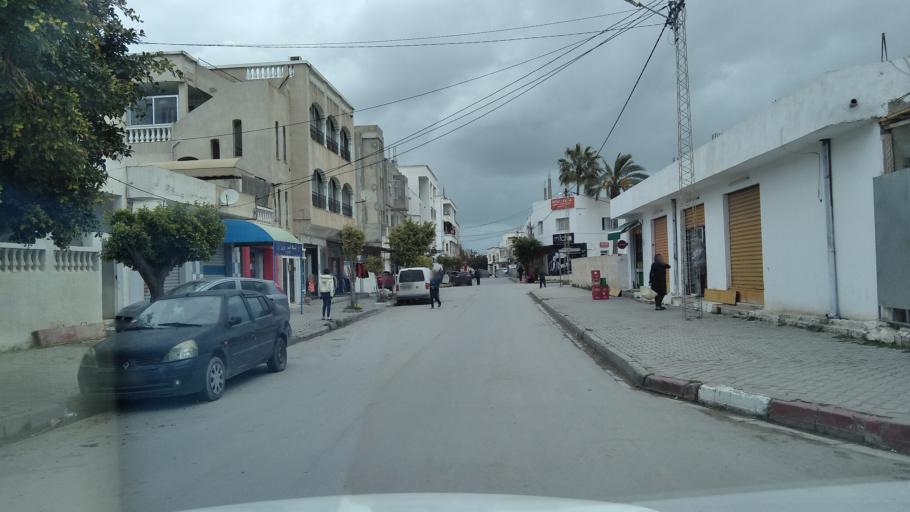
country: TN
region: Bin 'Arus
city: Ben Arous
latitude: 36.7586
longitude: 10.2248
